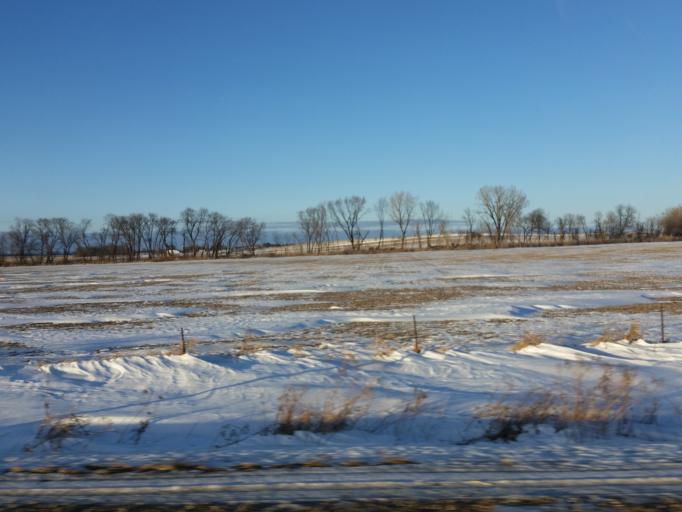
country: US
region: Iowa
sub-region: Butler County
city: Allison
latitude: 42.7448
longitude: -92.9013
